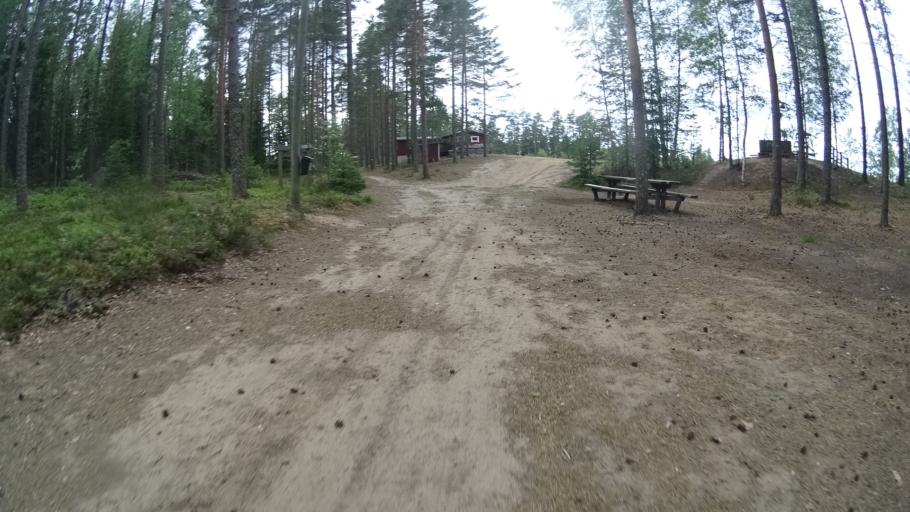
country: FI
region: Satakunta
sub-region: Pohjois-Satakunta
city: Jaemijaervi
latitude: 61.7709
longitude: 22.7507
